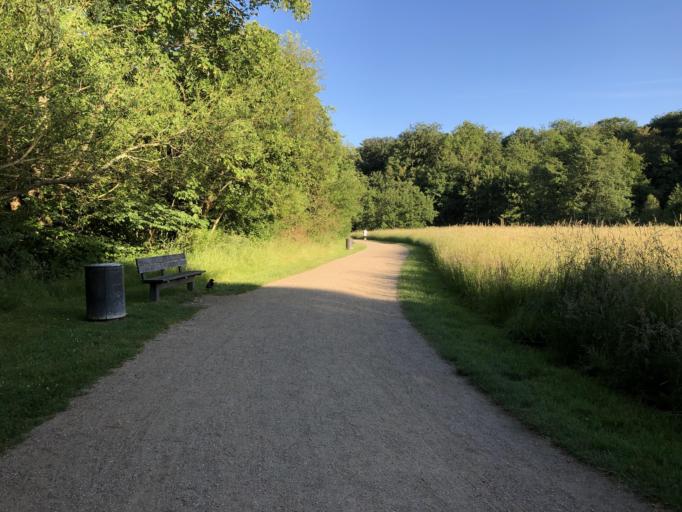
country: DK
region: South Denmark
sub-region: Odense Kommune
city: Odense
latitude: 55.3734
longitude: 10.3787
